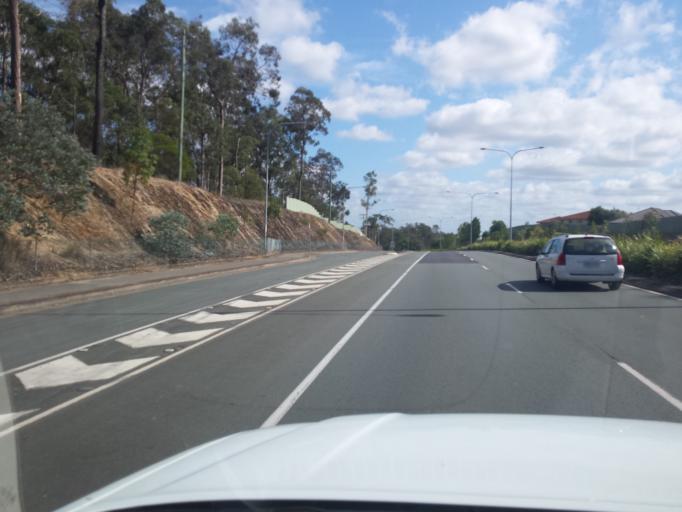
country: AU
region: Queensland
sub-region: Brisbane
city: Bridegman Downs
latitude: -27.3735
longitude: 152.9803
